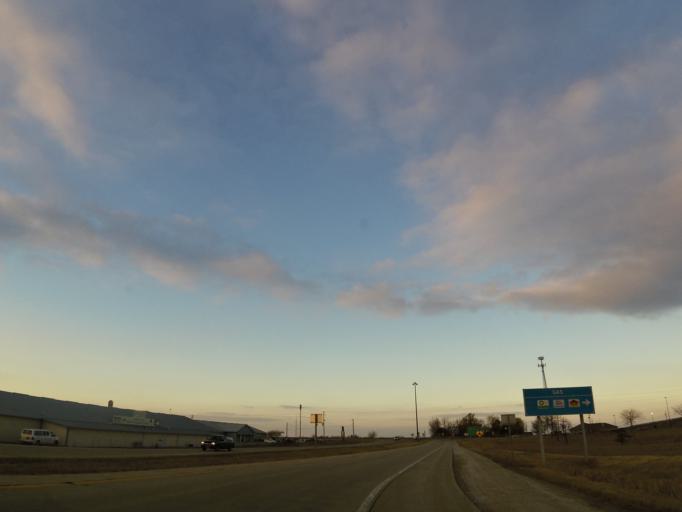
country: US
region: Illinois
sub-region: Woodford County
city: El Paso
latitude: 40.7343
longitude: -89.0371
